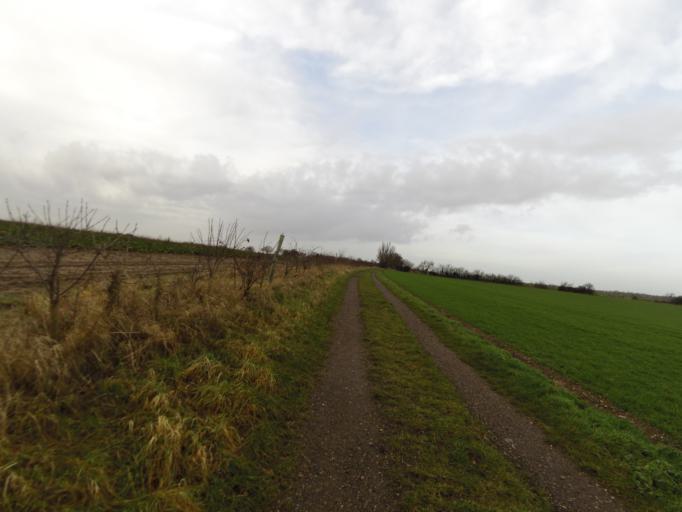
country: GB
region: England
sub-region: Suffolk
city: Needham Market
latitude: 52.1551
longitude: 1.0736
